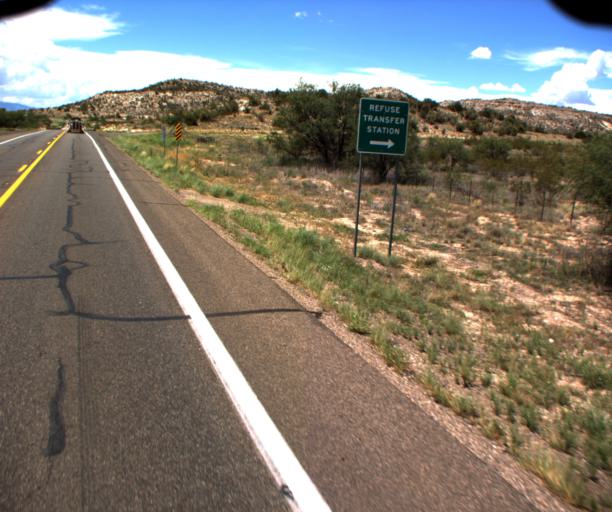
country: US
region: Arizona
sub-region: Yavapai County
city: Camp Verde
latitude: 34.5304
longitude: -111.8087
